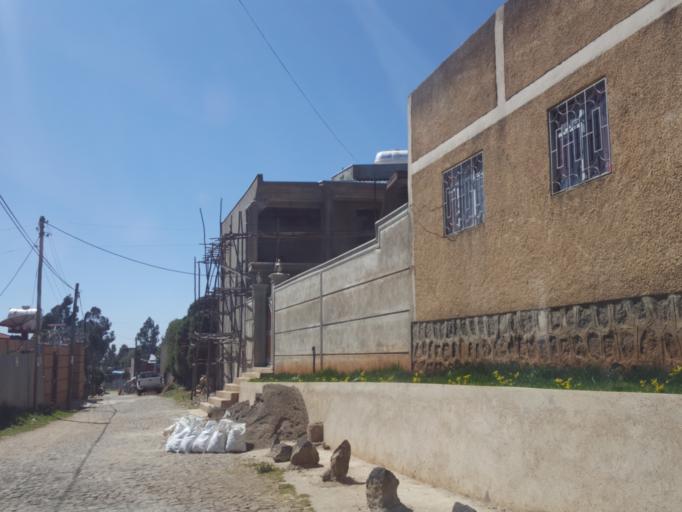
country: ET
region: Adis Abeba
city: Addis Ababa
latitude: 9.0603
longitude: 38.7456
